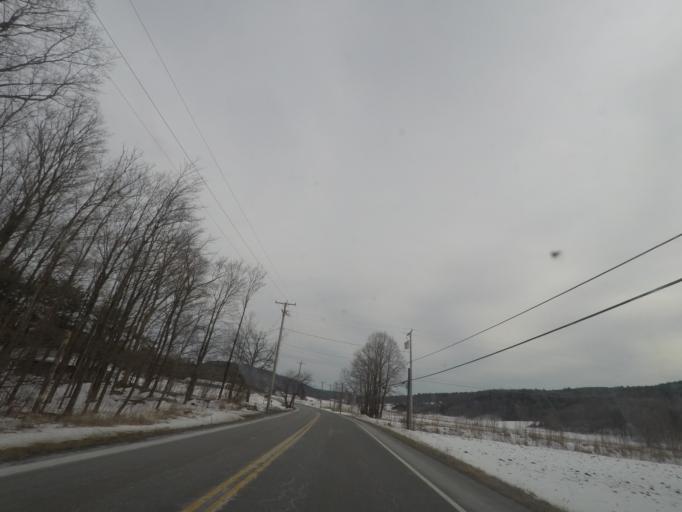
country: US
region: New York
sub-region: Albany County
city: Voorheesville
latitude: 42.5822
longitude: -73.9811
